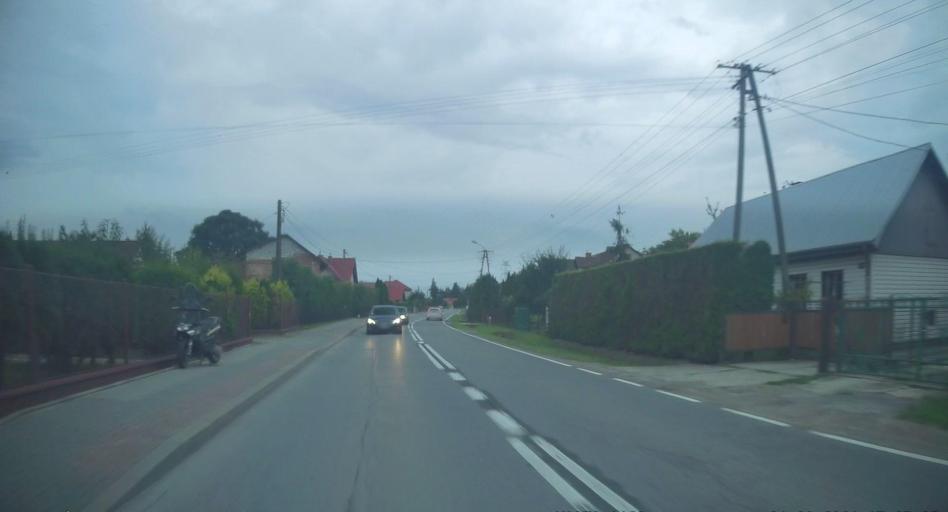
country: PL
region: Lesser Poland Voivodeship
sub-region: Powiat tarnowski
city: Wojnicz
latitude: 49.9911
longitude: 20.8399
